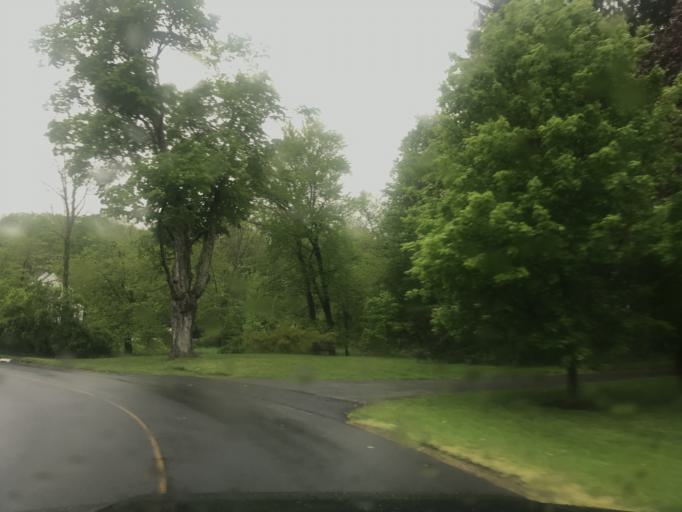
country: US
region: Connecticut
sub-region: Fairfield County
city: Bethel
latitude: 41.3055
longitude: -73.3803
